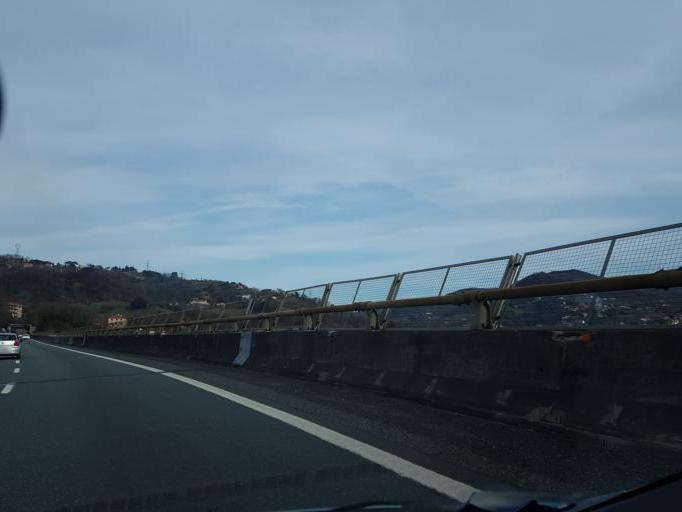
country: IT
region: Liguria
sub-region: Provincia di Genova
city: Manesseno
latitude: 44.4722
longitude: 8.9111
